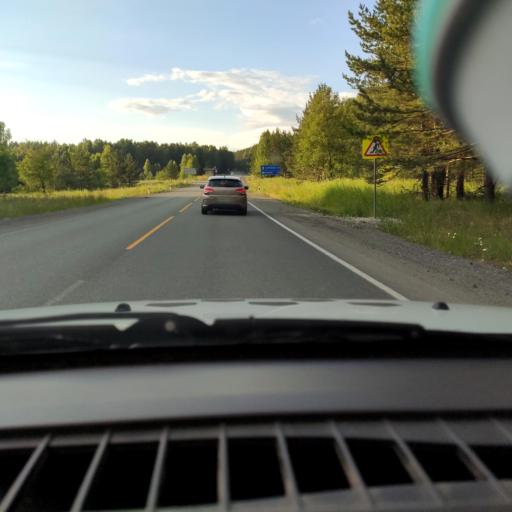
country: RU
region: Chelyabinsk
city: Turgoyak
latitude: 55.2647
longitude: 60.1972
